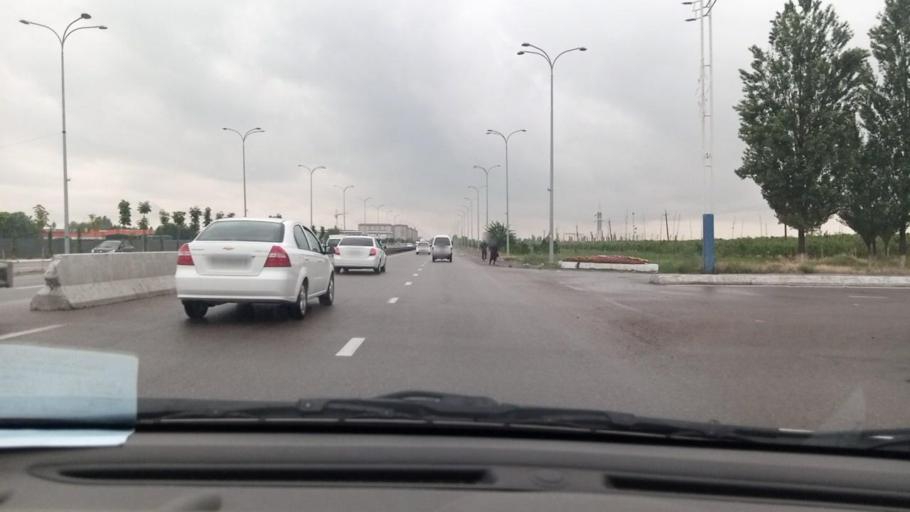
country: UZ
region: Toshkent
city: Ohangaron
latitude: 40.9107
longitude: 69.6205
